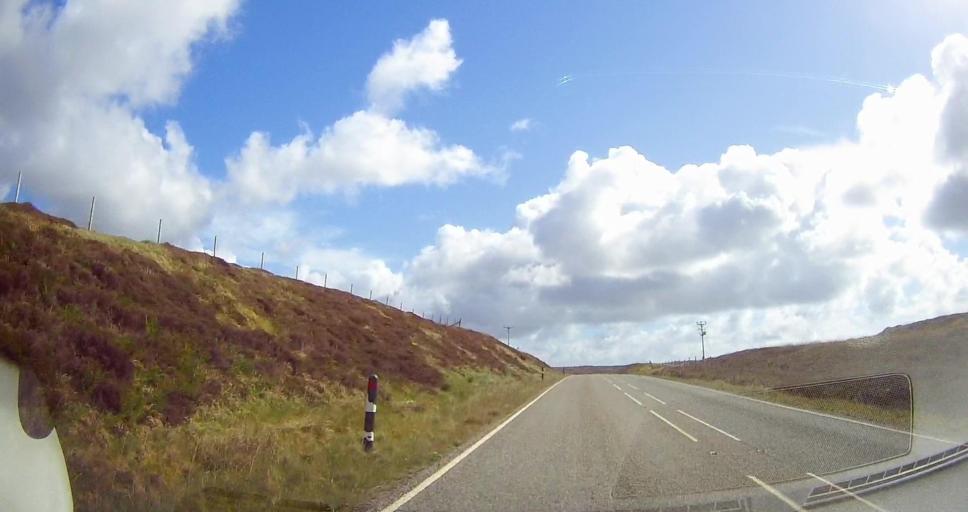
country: GB
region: Scotland
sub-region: Shetland Islands
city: Lerwick
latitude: 60.4709
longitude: -1.4068
